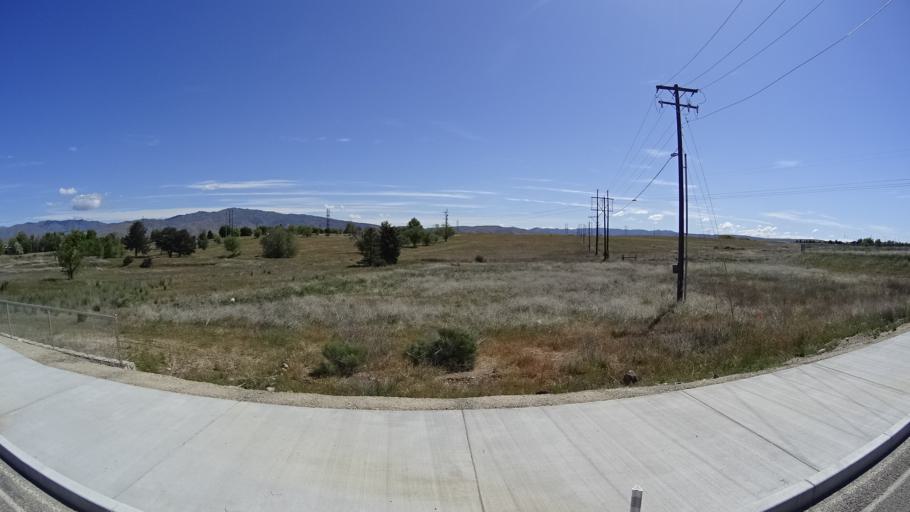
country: US
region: Idaho
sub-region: Ada County
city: Boise
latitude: 43.5384
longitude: -116.1546
